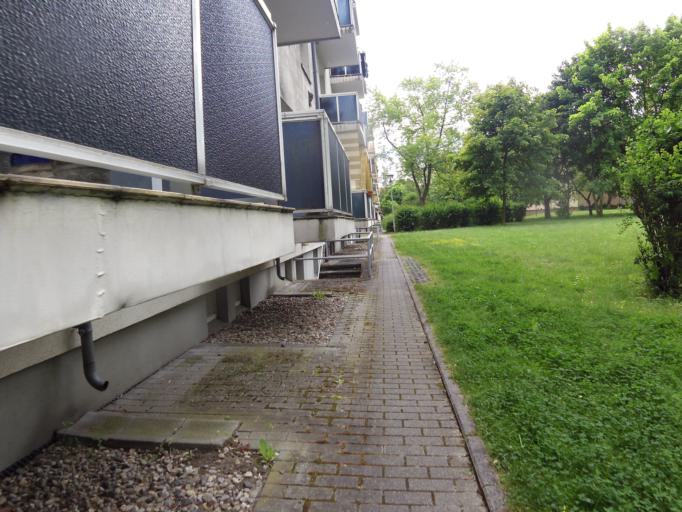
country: DE
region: Saxony
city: Leipzig
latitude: 51.3740
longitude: 12.3773
